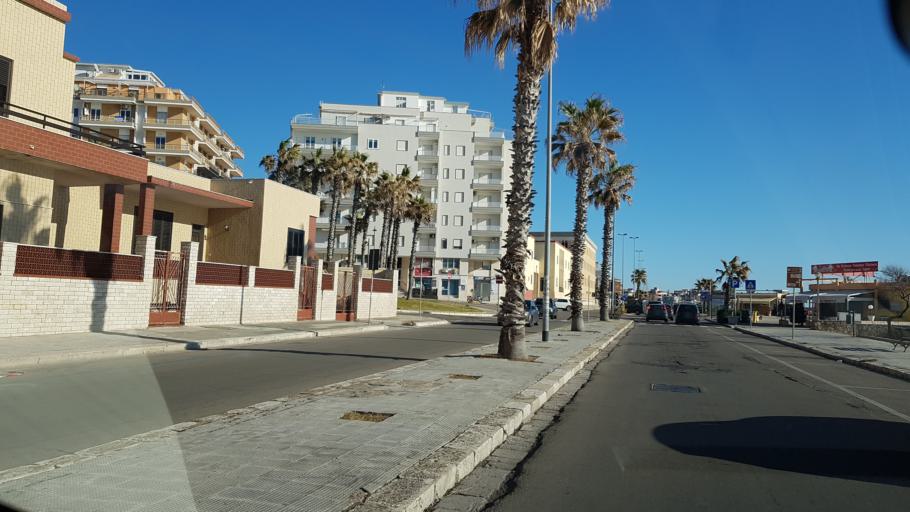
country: IT
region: Apulia
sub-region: Provincia di Lecce
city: Gallipoli
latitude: 40.0533
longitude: 17.9916
